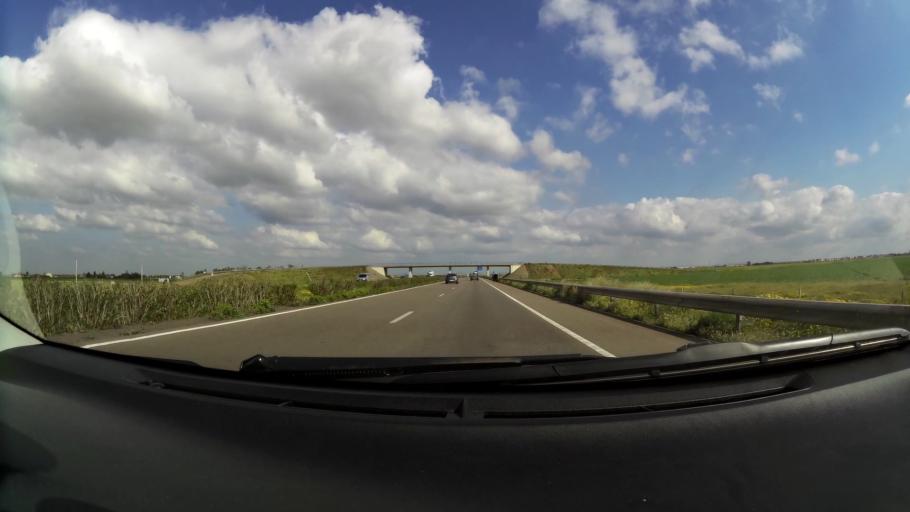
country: MA
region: Chaouia-Ouardigha
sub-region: Settat Province
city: Berrechid
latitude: 33.3073
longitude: -7.5864
